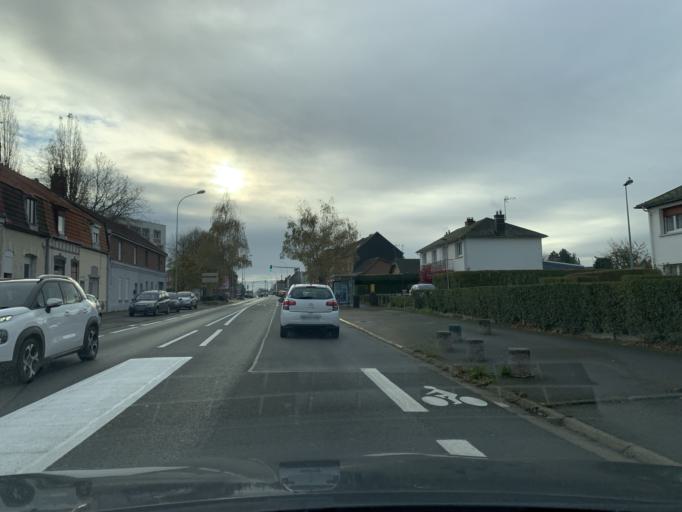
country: FR
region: Nord-Pas-de-Calais
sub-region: Departement du Nord
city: Lambres-lez-Douai
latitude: 50.3511
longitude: 3.0866
